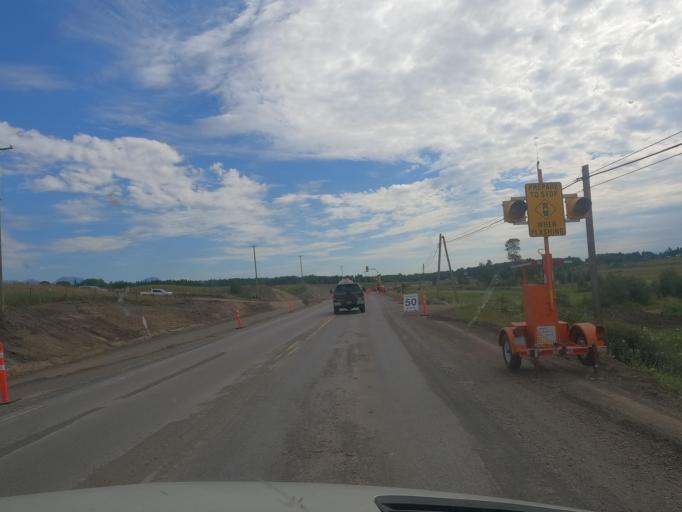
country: CA
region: British Columbia
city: Smithers
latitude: 54.8667
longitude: -127.2356
